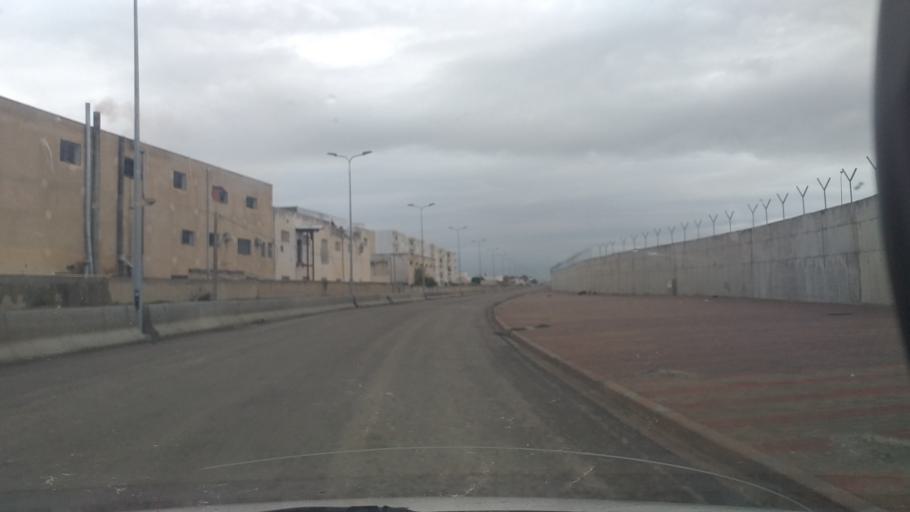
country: TN
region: Ariana
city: Ariana
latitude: 36.8607
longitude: 10.2154
